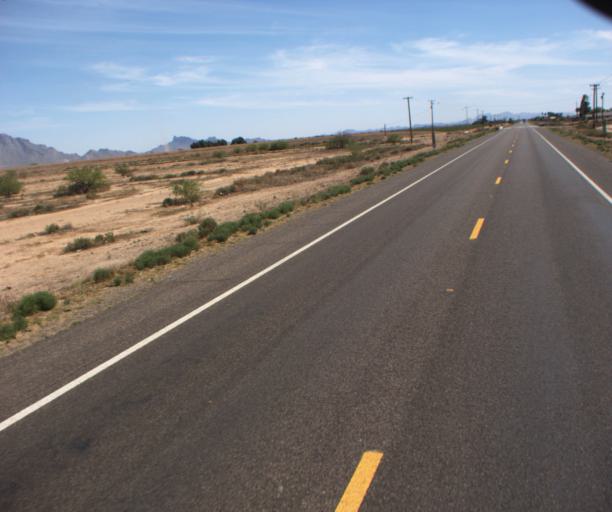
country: US
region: Arizona
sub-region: Pinal County
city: Eloy
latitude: 32.7942
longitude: -111.5154
